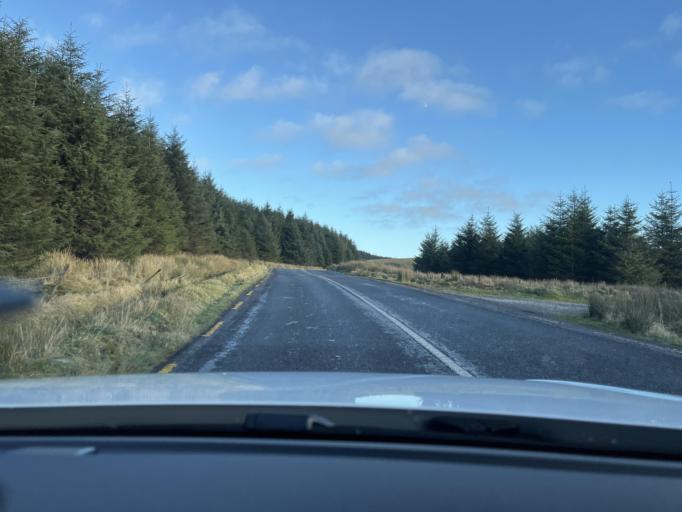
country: IE
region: Ulster
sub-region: An Cabhan
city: Ballyconnell
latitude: 54.1702
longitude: -7.8345
